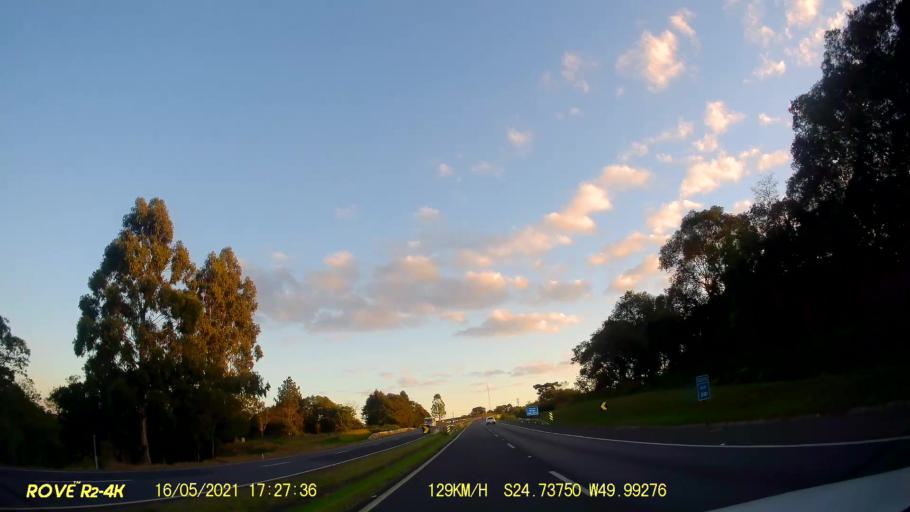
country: BR
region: Parana
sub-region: Castro
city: Castro
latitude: -24.7379
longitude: -49.9929
